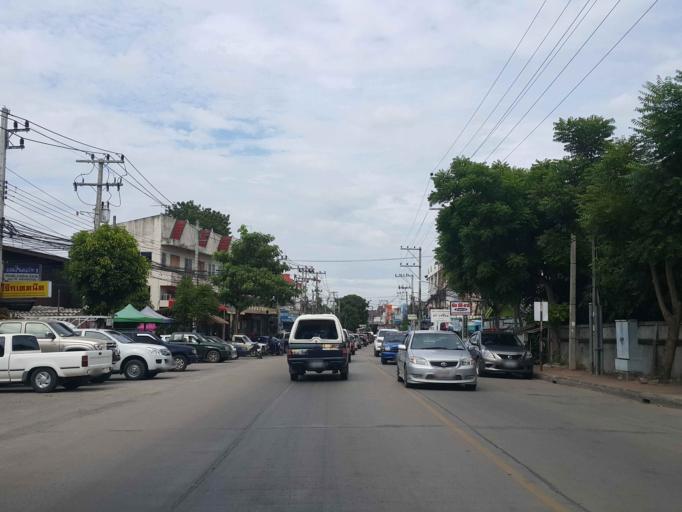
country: TH
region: Lamphun
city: Lamphun
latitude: 18.5713
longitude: 98.9990
